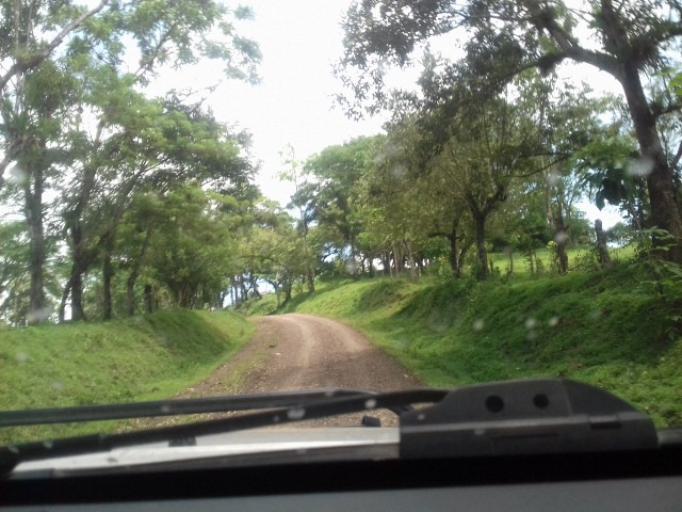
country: NI
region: Matagalpa
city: Rio Blanco
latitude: 12.9786
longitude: -85.3713
